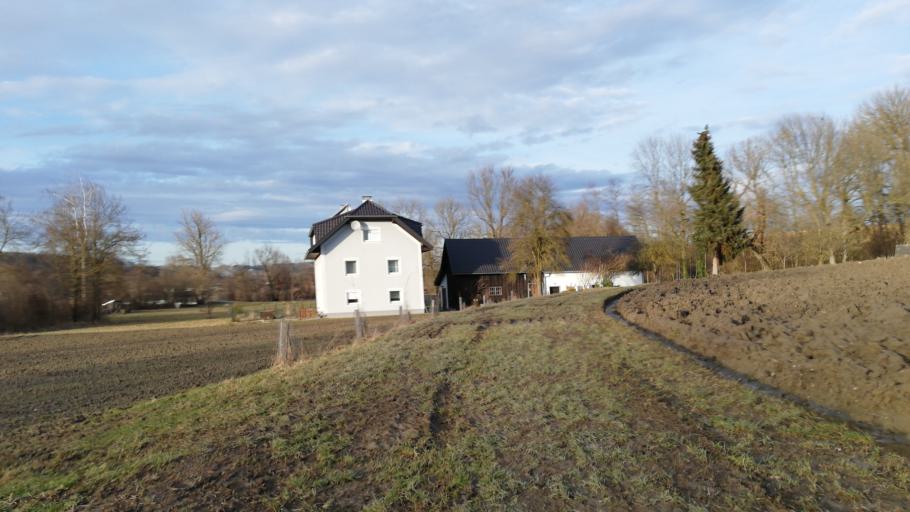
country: AT
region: Upper Austria
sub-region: Politischer Bezirk Grieskirchen
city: Bad Schallerbach
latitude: 48.2023
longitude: 13.9302
